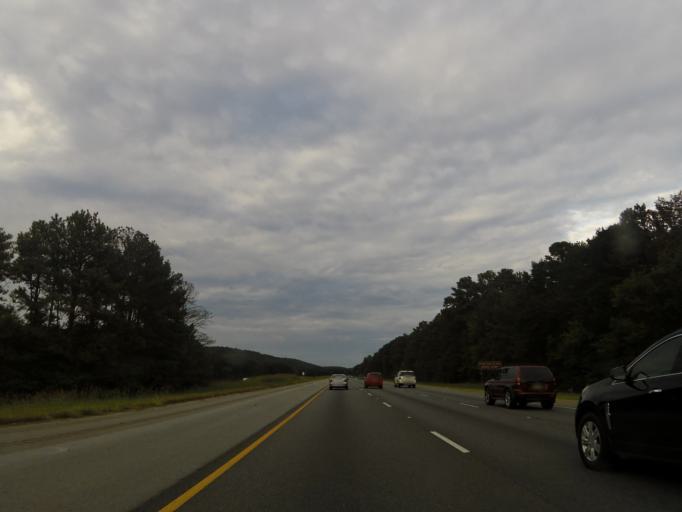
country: US
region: Alabama
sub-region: Shelby County
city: Pelham
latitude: 33.2908
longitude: -86.7988
